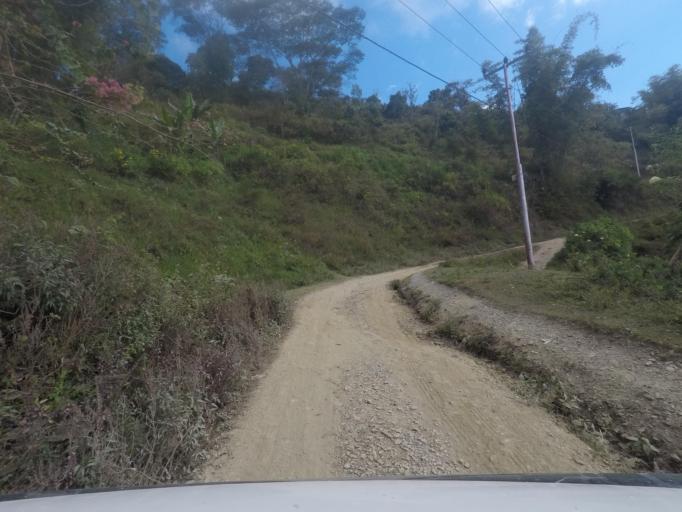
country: TL
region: Ermera
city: Gleno
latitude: -8.7516
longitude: 125.3249
